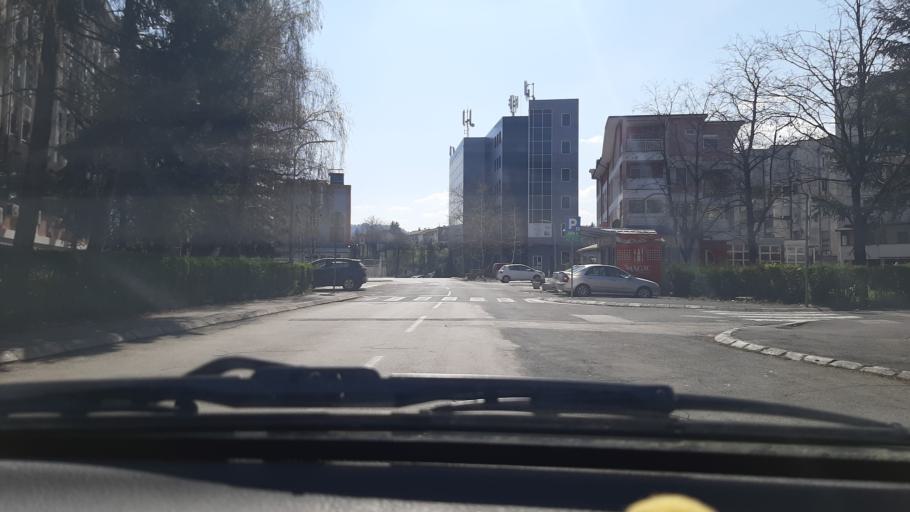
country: BA
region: Republika Srpska
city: Banja Luka
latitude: 44.7727
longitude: 17.1829
